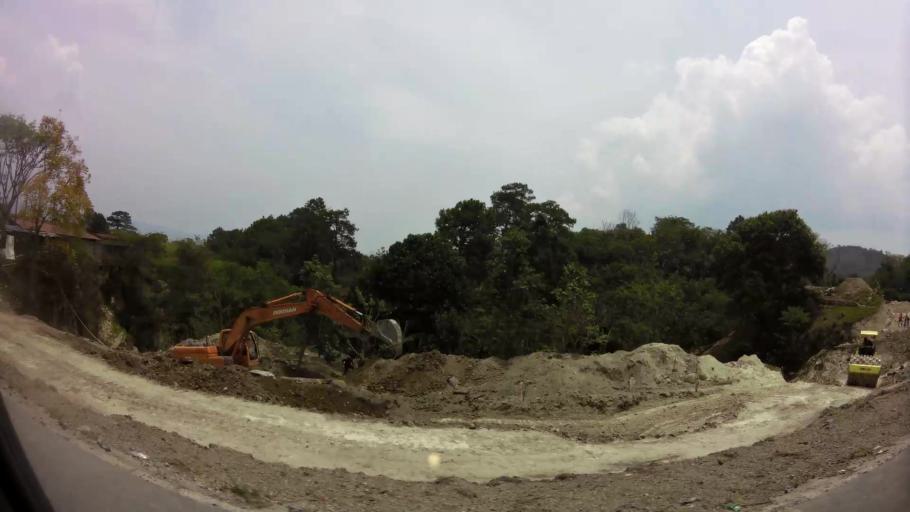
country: HN
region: Comayagua
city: Taulabe
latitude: 14.6736
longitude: -87.9493
